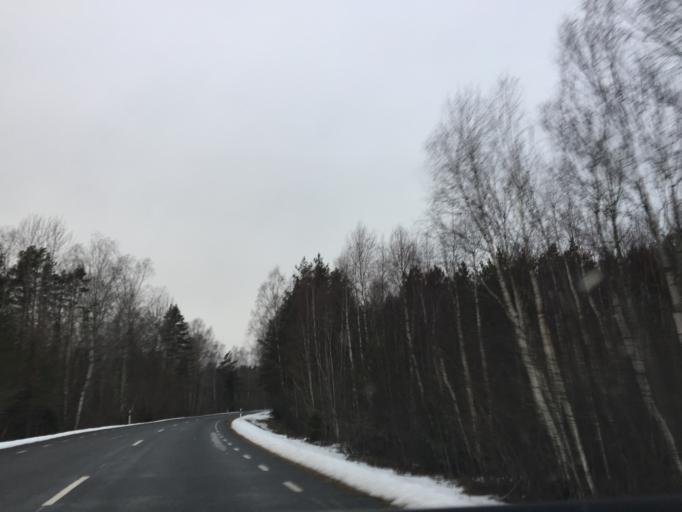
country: EE
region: Saare
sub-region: Kuressaare linn
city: Kuressaare
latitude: 58.5533
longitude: 22.3213
